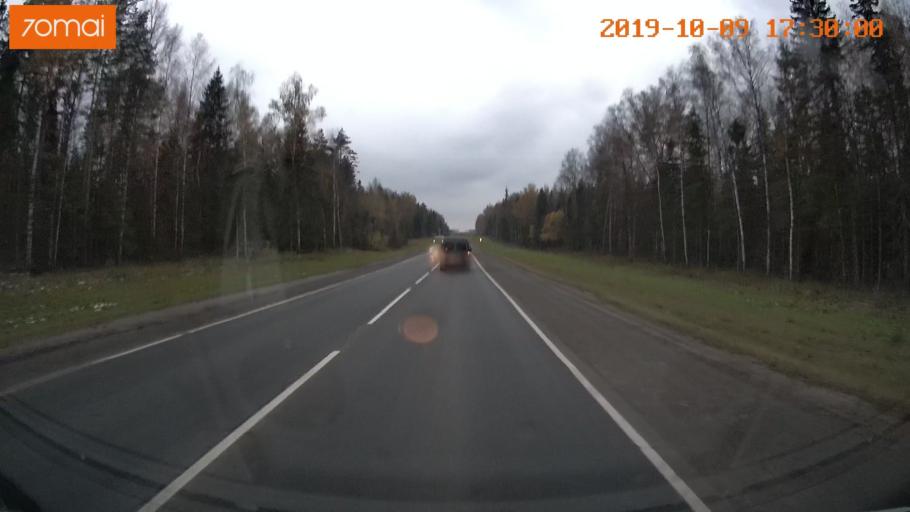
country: RU
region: Ivanovo
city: Bogorodskoye
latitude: 57.1459
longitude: 41.0537
